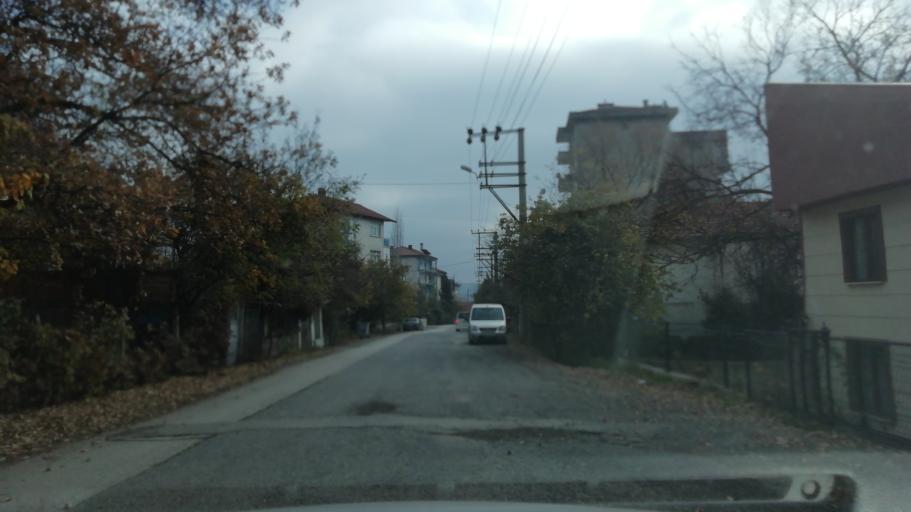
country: TR
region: Karabuk
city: Karabuk
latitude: 41.2231
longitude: 32.6258
